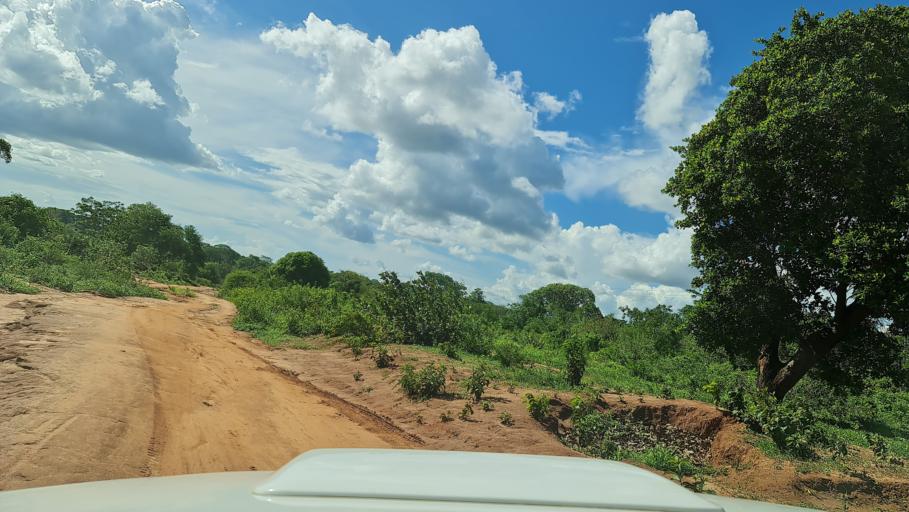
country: MZ
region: Nampula
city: Ilha de Mocambique
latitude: -15.4178
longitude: 40.2620
